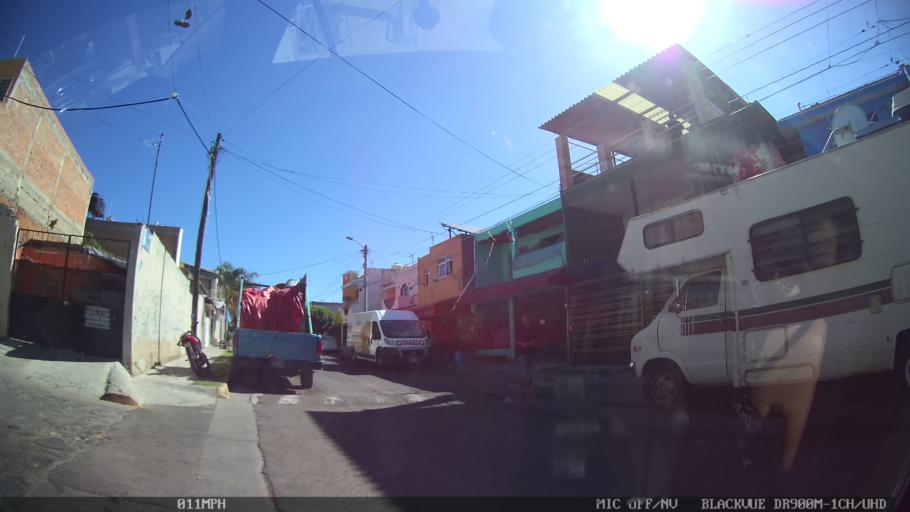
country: MX
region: Jalisco
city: Tlaquepaque
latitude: 20.6839
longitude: -103.2768
